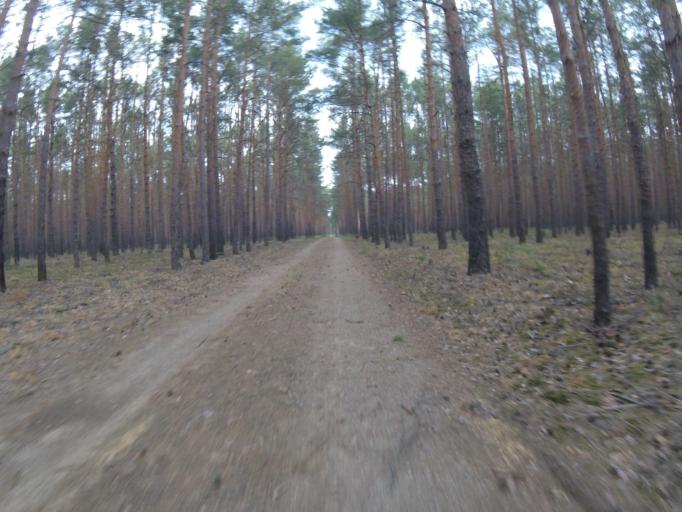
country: DE
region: Brandenburg
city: Halbe
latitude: 52.1088
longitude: 13.7208
